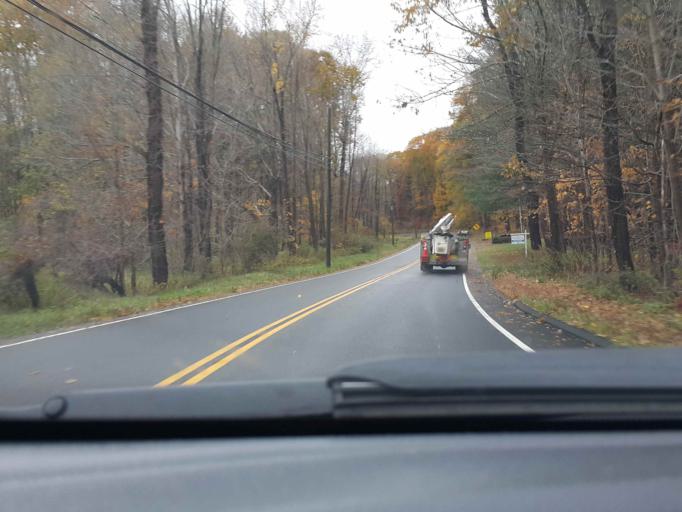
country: US
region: Connecticut
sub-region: Middlesex County
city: Durham
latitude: 41.4037
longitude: -72.6967
